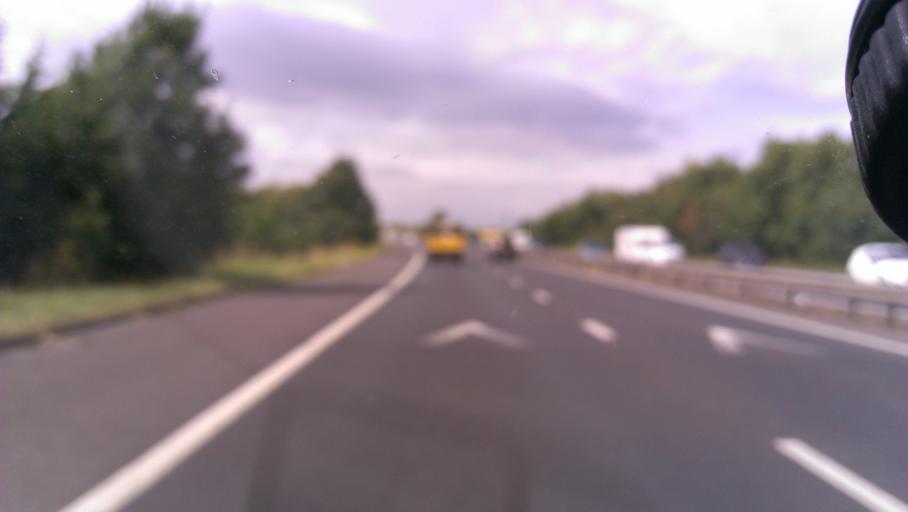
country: GB
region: England
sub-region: Cambridgeshire
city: Duxford
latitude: 52.1188
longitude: 0.1264
